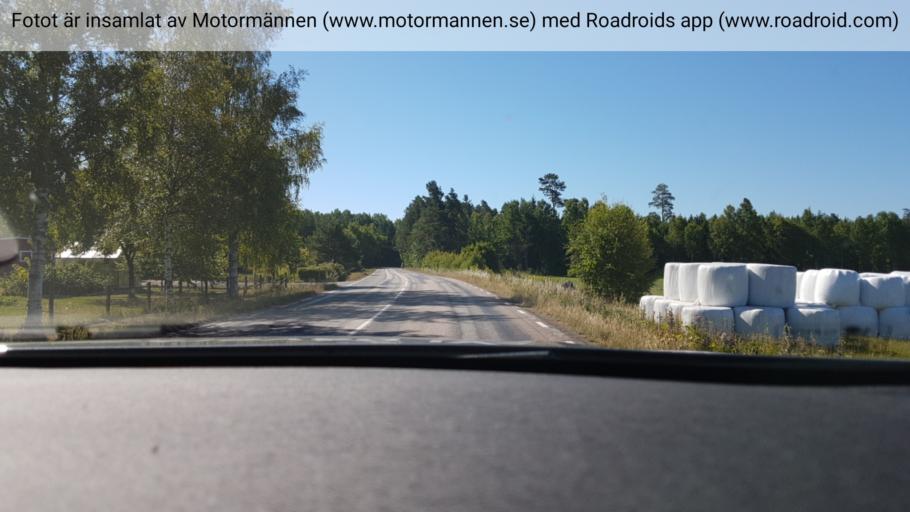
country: SE
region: Vaestra Goetaland
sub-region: Tidaholms Kommun
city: Tidaholm
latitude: 58.1511
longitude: 13.9652
